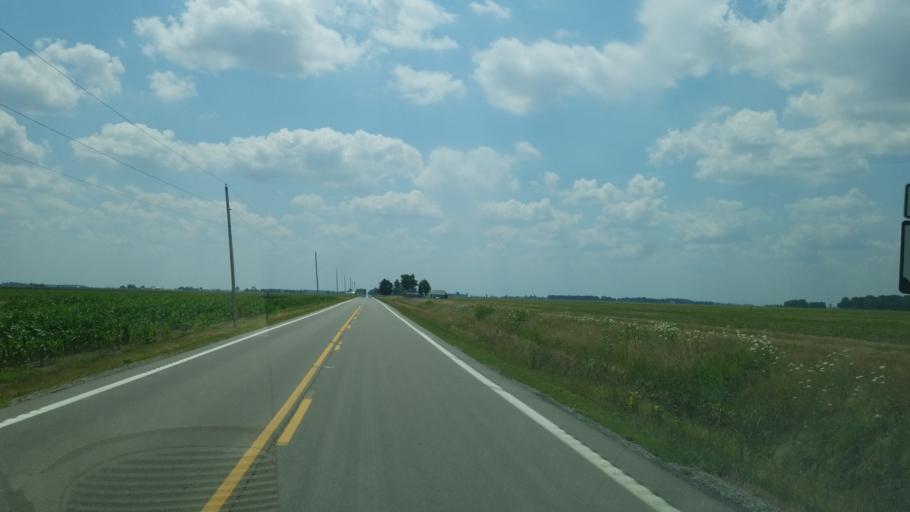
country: US
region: Ohio
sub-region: Henry County
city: Deshler
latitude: 41.3272
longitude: -83.9414
